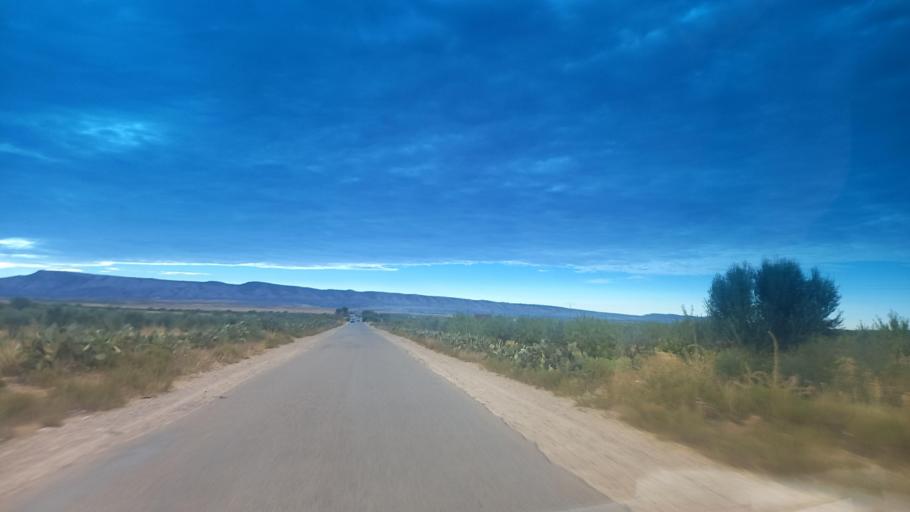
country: TN
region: Al Qasrayn
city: Sbiba
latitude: 35.3689
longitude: 9.0784
